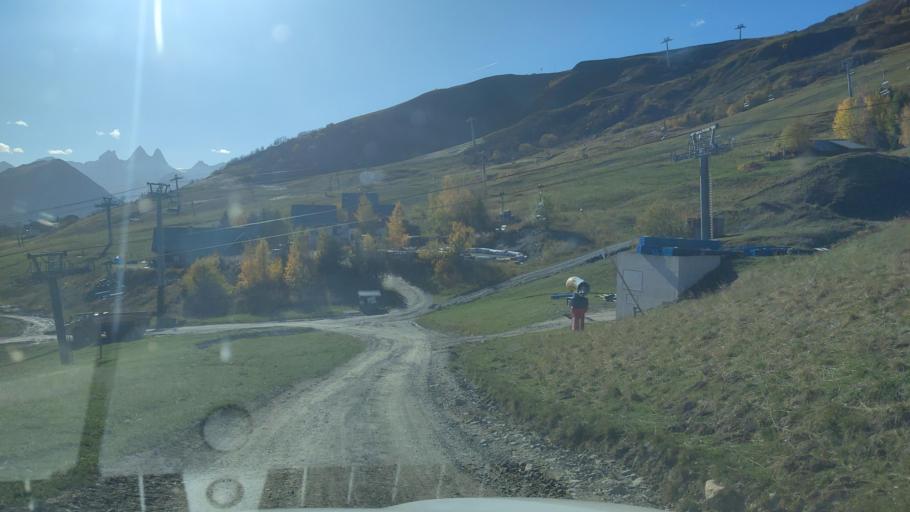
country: FR
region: Rhone-Alpes
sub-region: Departement de la Savoie
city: Saint-Etienne-de-Cuines
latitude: 45.2574
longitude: 6.2518
